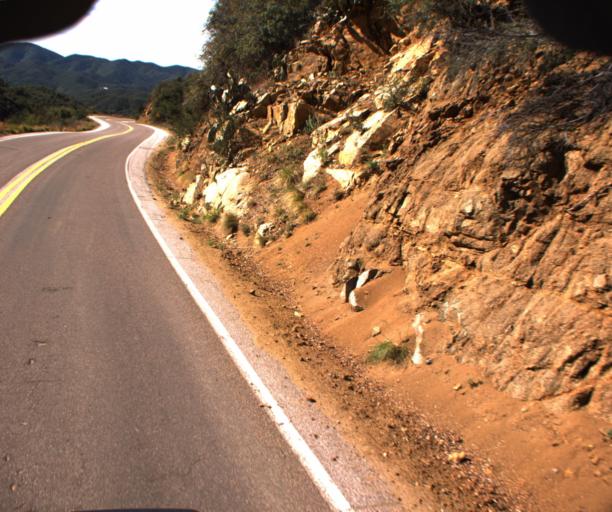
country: US
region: Arizona
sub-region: Yavapai County
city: Prescott
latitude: 34.4585
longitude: -112.5240
